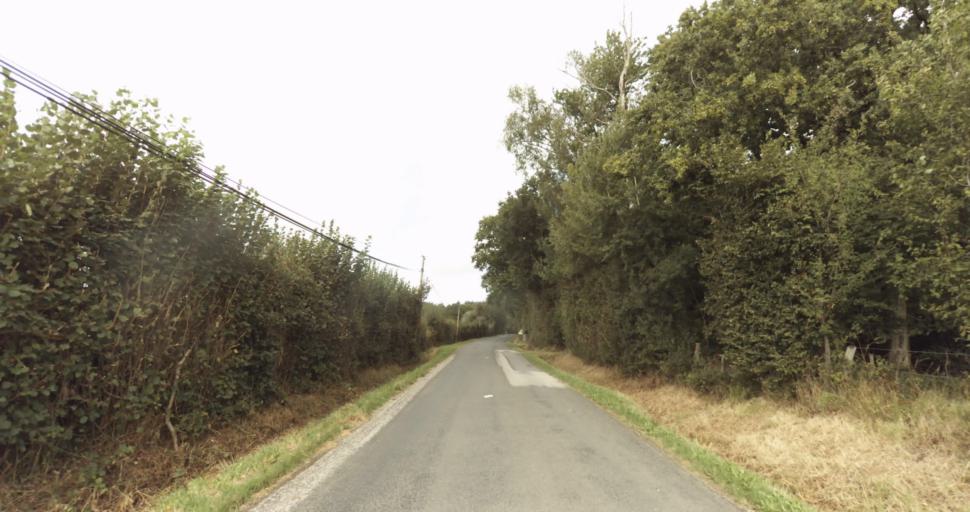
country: FR
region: Lower Normandy
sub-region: Departement de l'Orne
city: Gace
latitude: 48.8045
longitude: 0.2522
